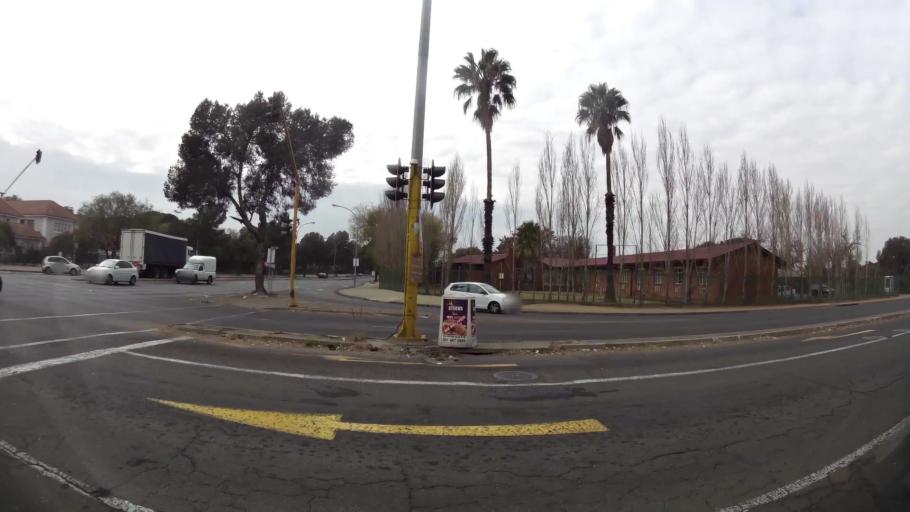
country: ZA
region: Orange Free State
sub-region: Mangaung Metropolitan Municipality
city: Bloemfontein
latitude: -29.1240
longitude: 26.2114
